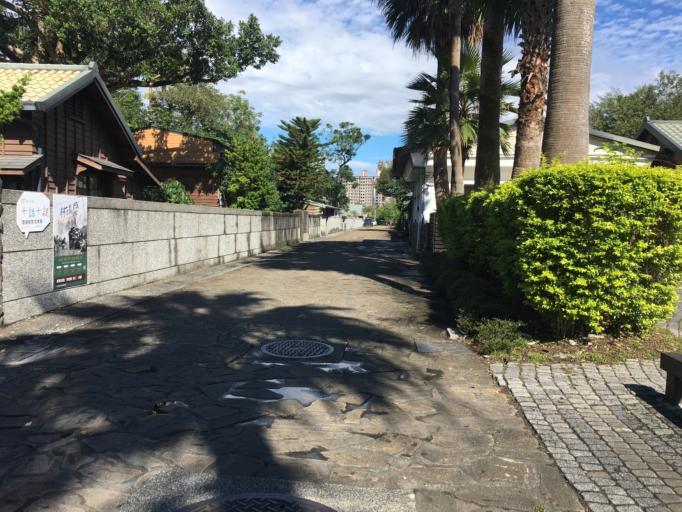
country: TW
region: Taiwan
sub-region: Yilan
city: Yilan
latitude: 24.6842
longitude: 121.7715
